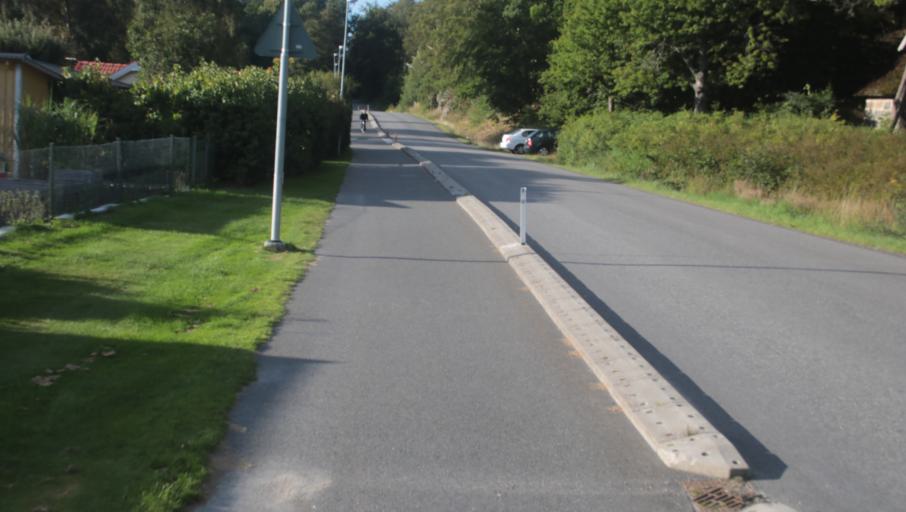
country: SE
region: Blekinge
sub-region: Karlshamns Kommun
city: Karlshamn
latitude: 56.1634
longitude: 14.8982
